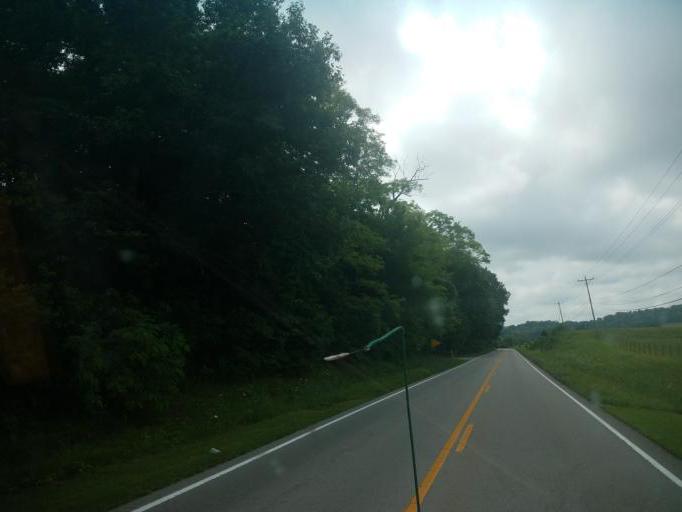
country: US
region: Kentucky
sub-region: Clinton County
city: Albany
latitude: 36.7727
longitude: -85.1712
